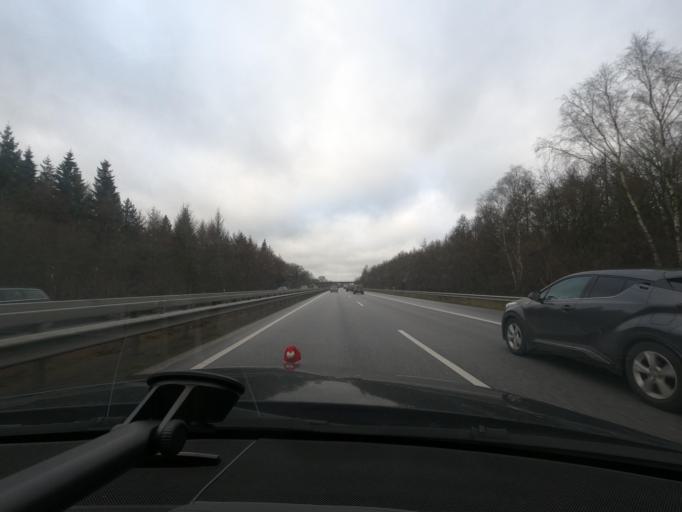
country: DE
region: Schleswig-Holstein
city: Emkendorf
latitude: 54.2351
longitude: 9.8284
